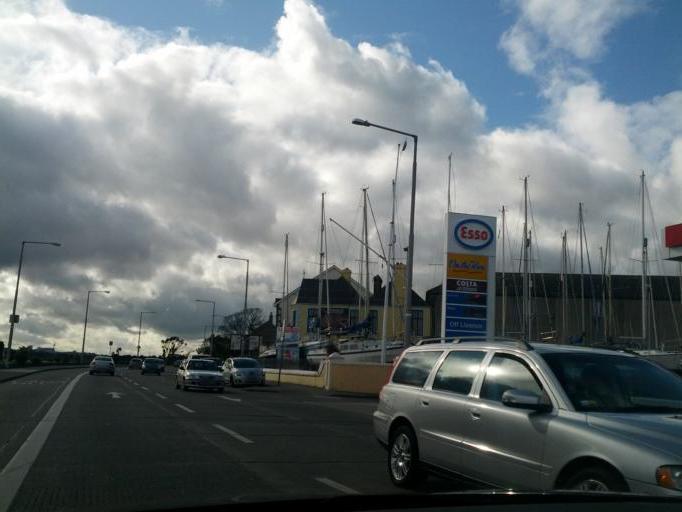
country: IE
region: Leinster
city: Dollymount
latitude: 53.3584
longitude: -6.1912
